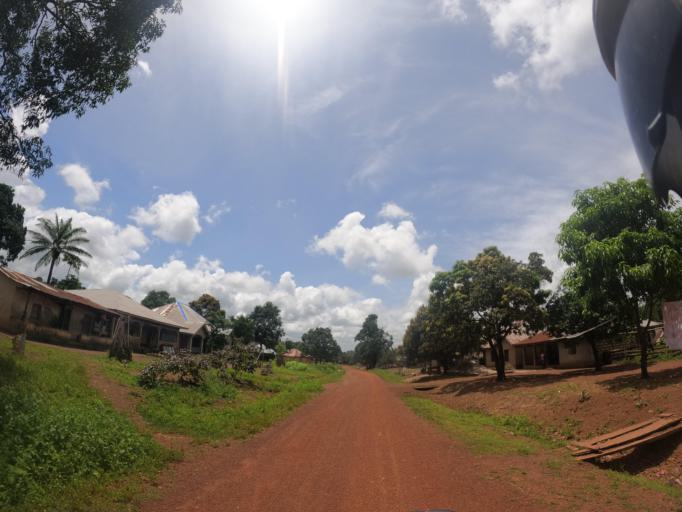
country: SL
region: Northern Province
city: Makeni
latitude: 9.1254
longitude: -12.2551
